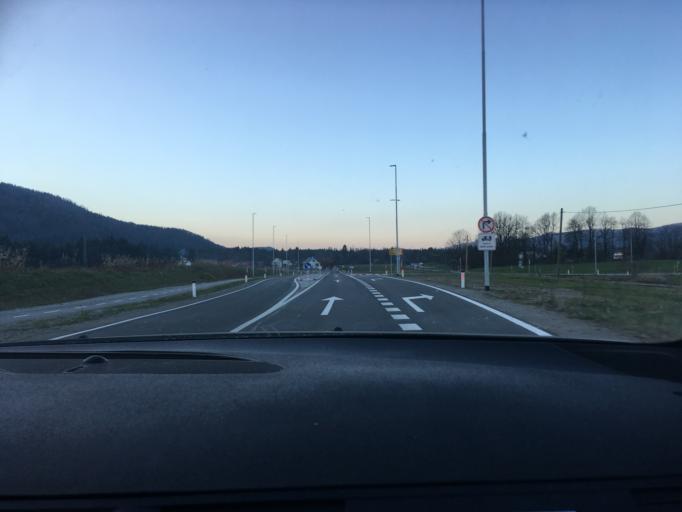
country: SI
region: Kocevje
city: Kocevje
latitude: 45.6713
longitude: 14.8351
